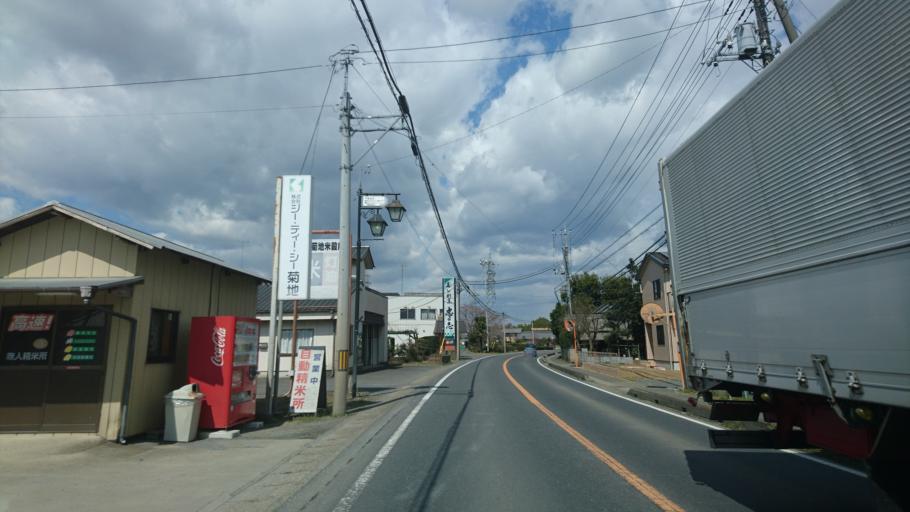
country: JP
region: Ibaraki
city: Ishige
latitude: 36.2072
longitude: 139.9404
